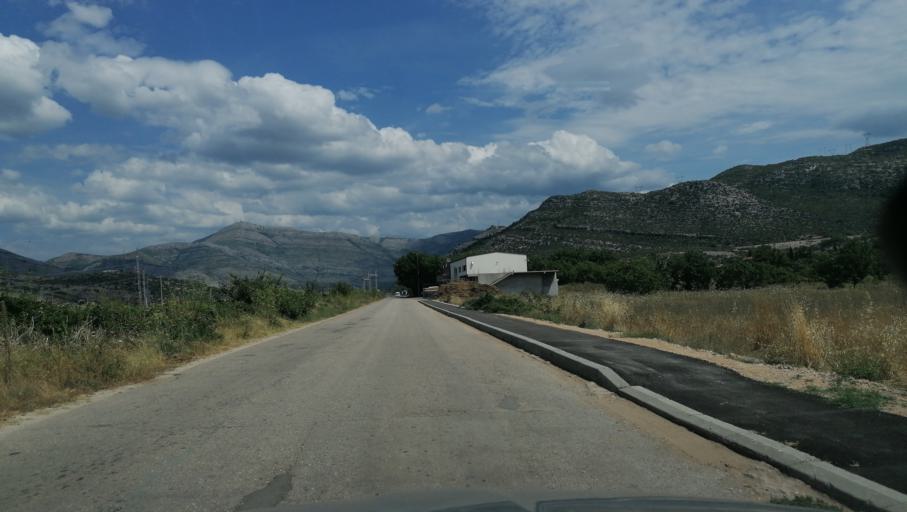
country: BA
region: Republika Srpska
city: Trebinje
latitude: 42.6725
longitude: 18.3292
